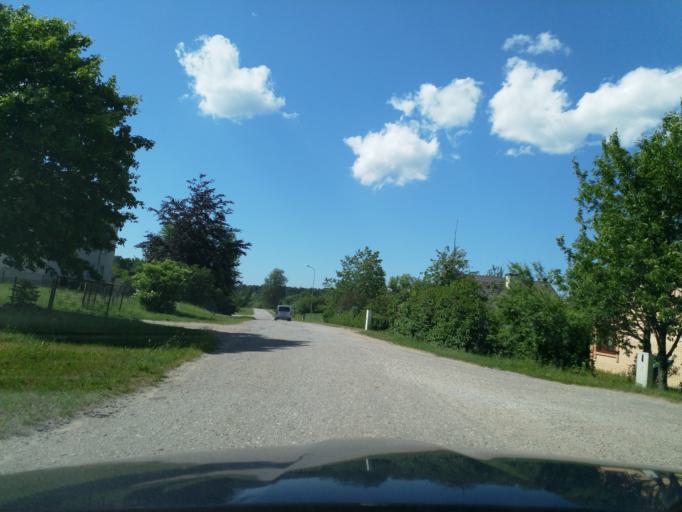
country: LV
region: Alsunga
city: Alsunga
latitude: 56.9751
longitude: 21.5657
